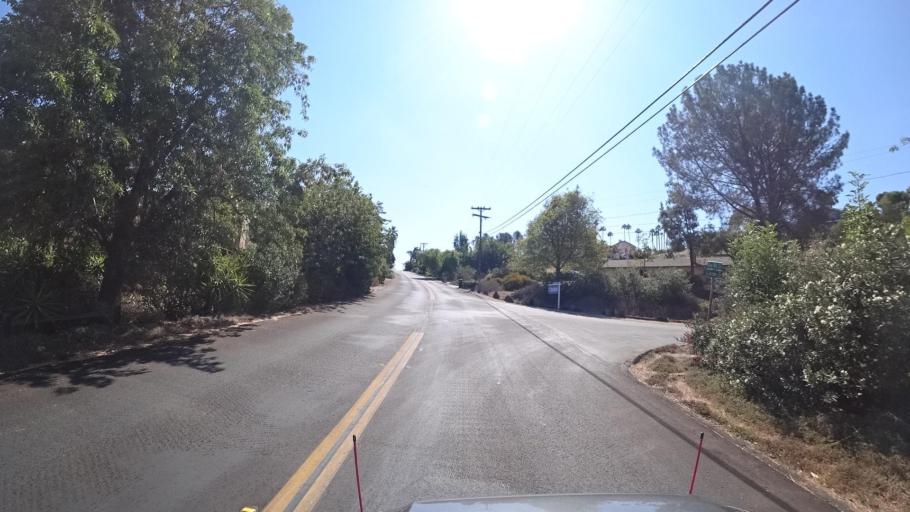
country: US
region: California
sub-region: San Diego County
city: Winter Gardens
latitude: 32.8324
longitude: -116.9253
